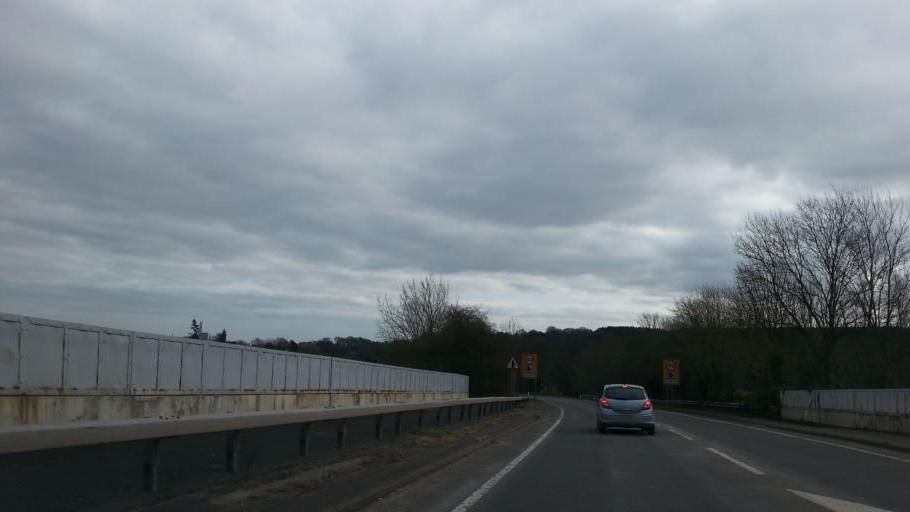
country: GB
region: England
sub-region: Staffordshire
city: Colwich
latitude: 52.7894
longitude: -1.9823
